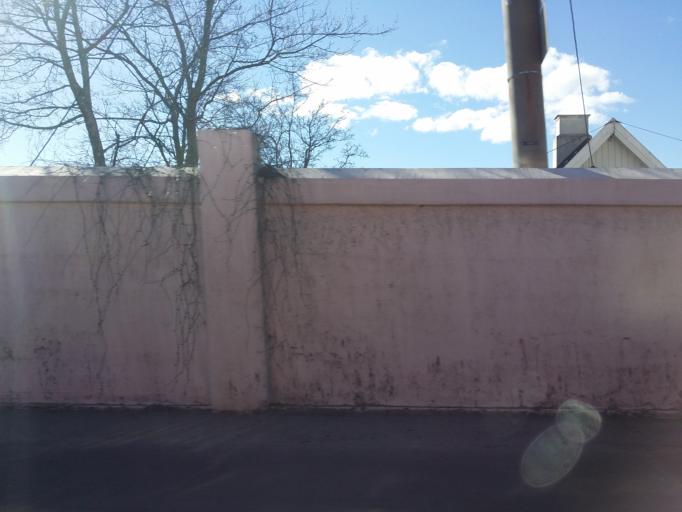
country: NO
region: Akershus
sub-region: Oppegard
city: Kolbotn
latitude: 59.8628
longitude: 10.7843
